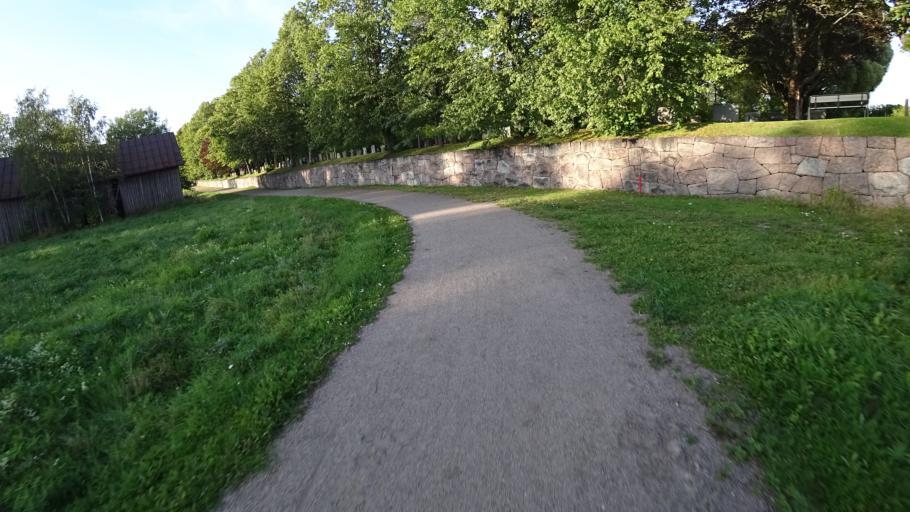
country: FI
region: Uusimaa
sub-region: Helsinki
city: Vantaa
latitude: 60.2815
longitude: 24.9854
